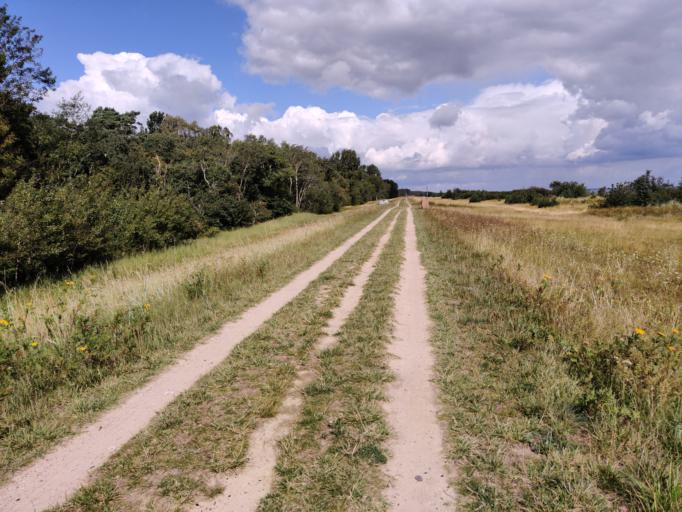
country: DK
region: Zealand
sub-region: Guldborgsund Kommune
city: Nykobing Falster
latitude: 54.6065
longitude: 11.9665
